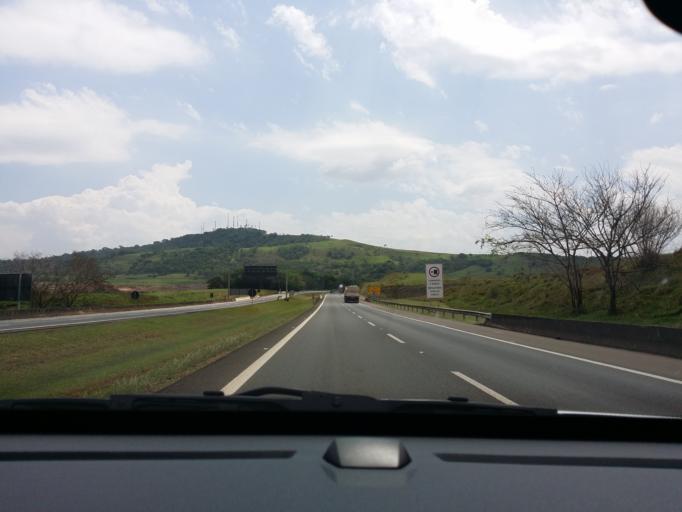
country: BR
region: Sao Paulo
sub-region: Limeira
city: Limeira
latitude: -22.5522
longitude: -47.4614
